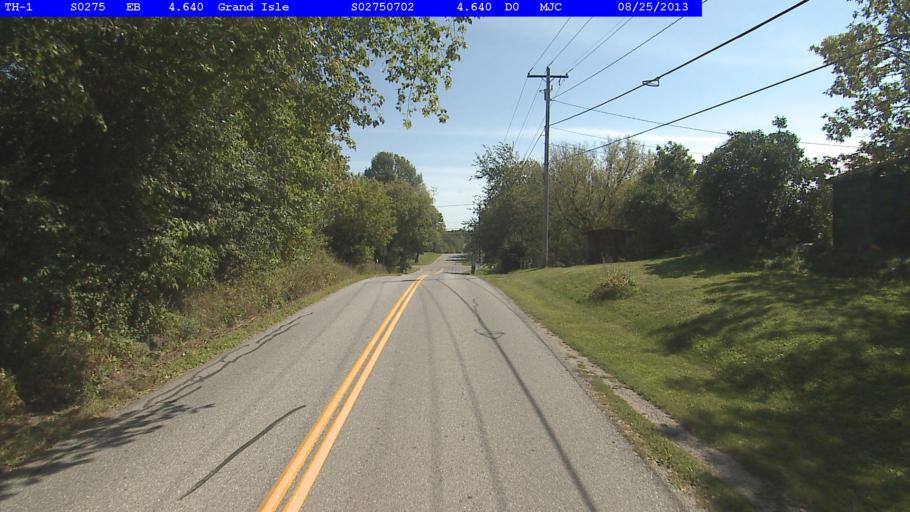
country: US
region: Vermont
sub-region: Grand Isle County
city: North Hero
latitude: 44.7414
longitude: -73.2907
